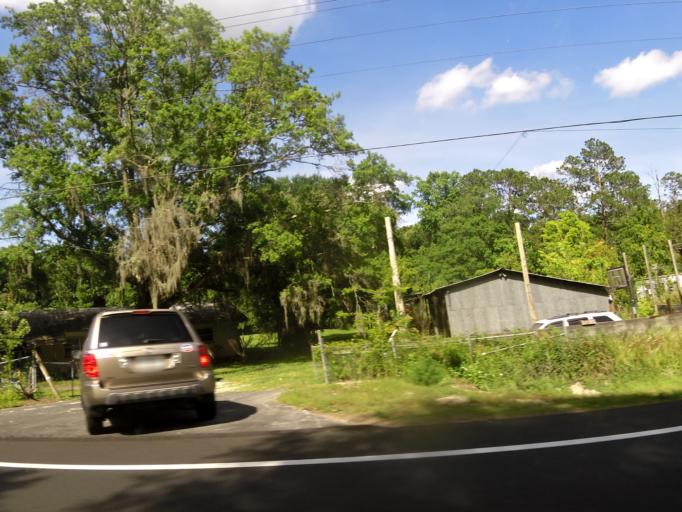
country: US
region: Florida
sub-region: Nassau County
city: Callahan
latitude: 30.5909
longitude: -81.8607
